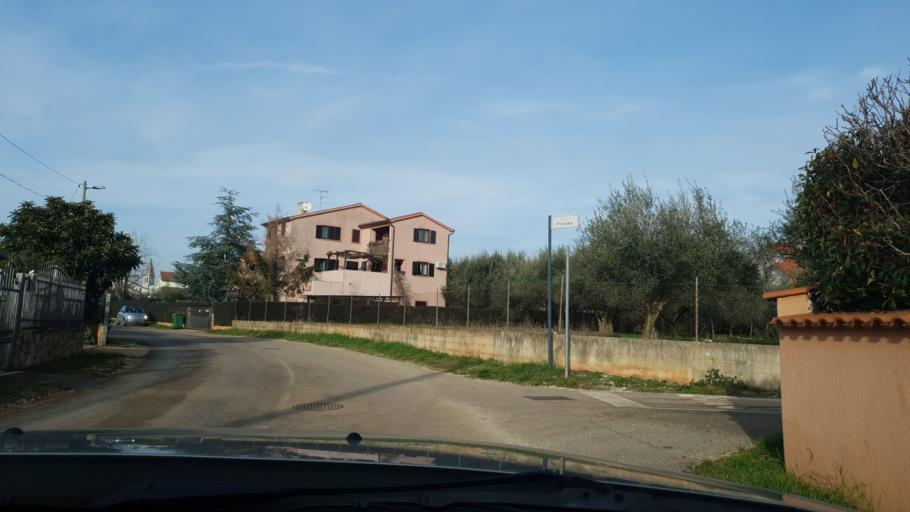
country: HR
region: Istarska
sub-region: Grad Porec
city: Porec
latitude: 45.2594
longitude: 13.6612
